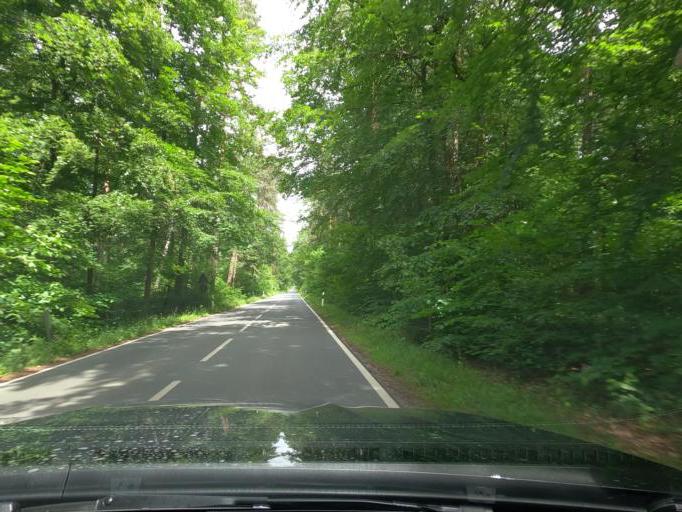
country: DE
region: Lower Saxony
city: Lehrte
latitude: 52.3971
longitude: 9.9258
